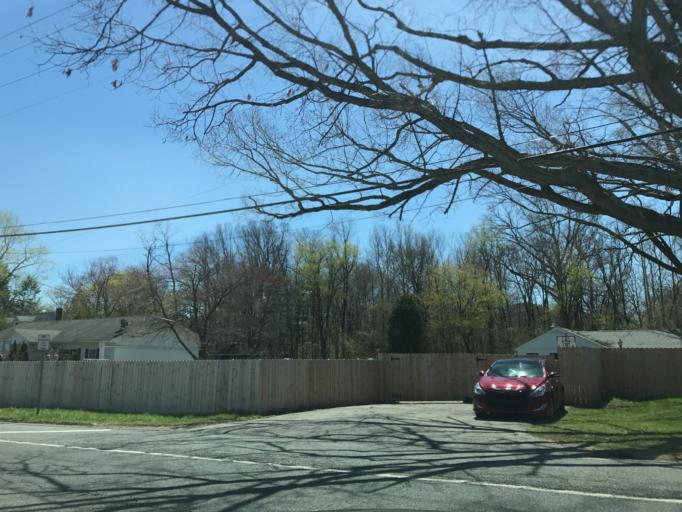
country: US
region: Maryland
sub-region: Anne Arundel County
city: Severn
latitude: 39.1372
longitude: -76.6901
